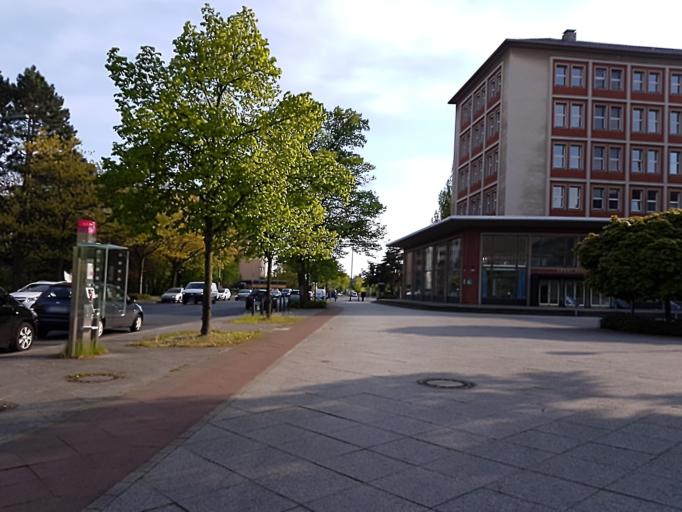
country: DE
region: Berlin
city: Wittenau
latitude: 52.5888
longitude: 13.3247
